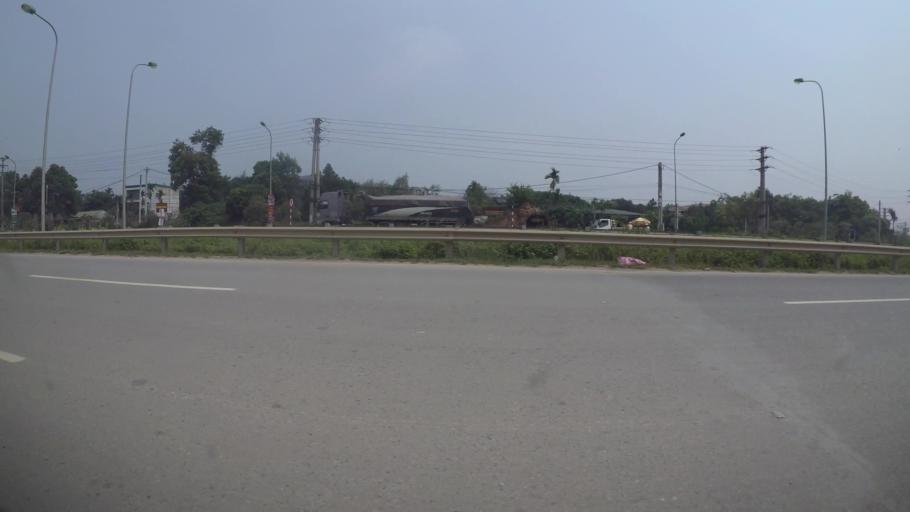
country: VN
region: Ha Noi
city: Lien Quan
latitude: 20.9900
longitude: 105.5200
